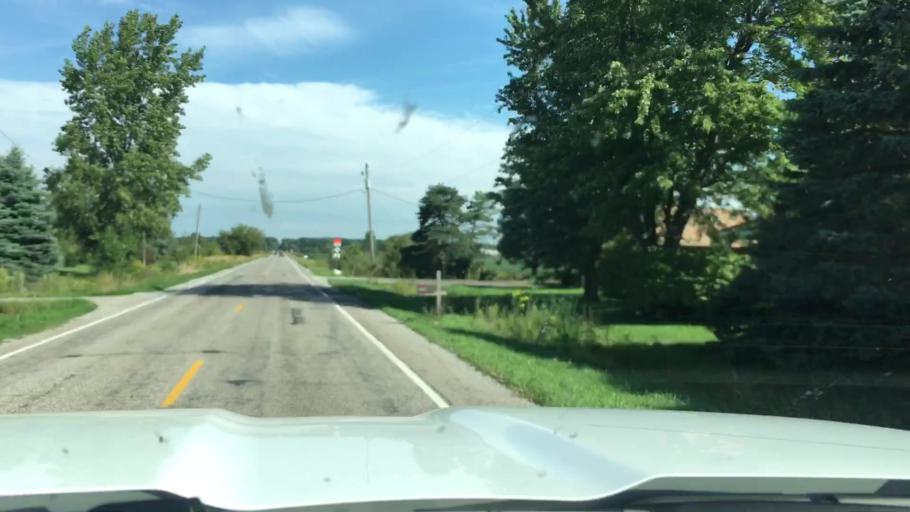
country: US
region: Michigan
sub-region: Saginaw County
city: Hemlock
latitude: 43.4436
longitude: -84.2301
